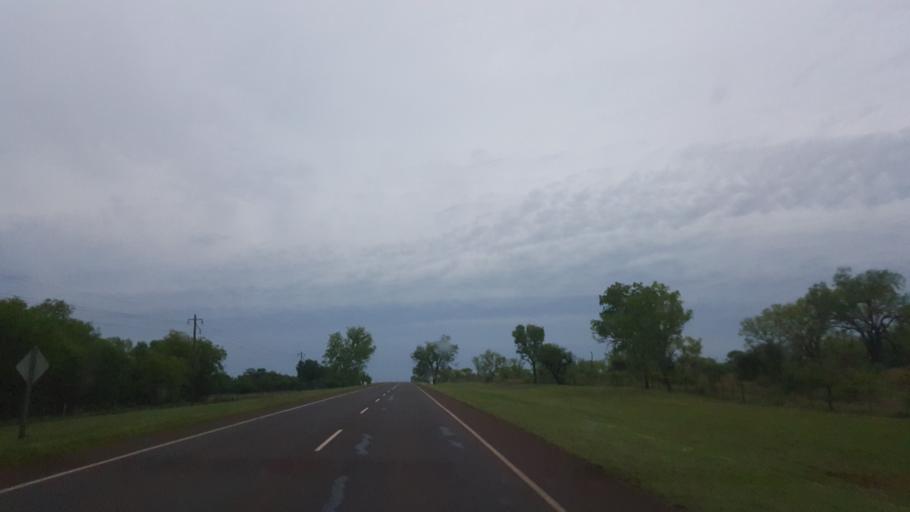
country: AR
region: Misiones
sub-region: Departamento de Apostoles
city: San Jose
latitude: -27.7194
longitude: -55.7928
